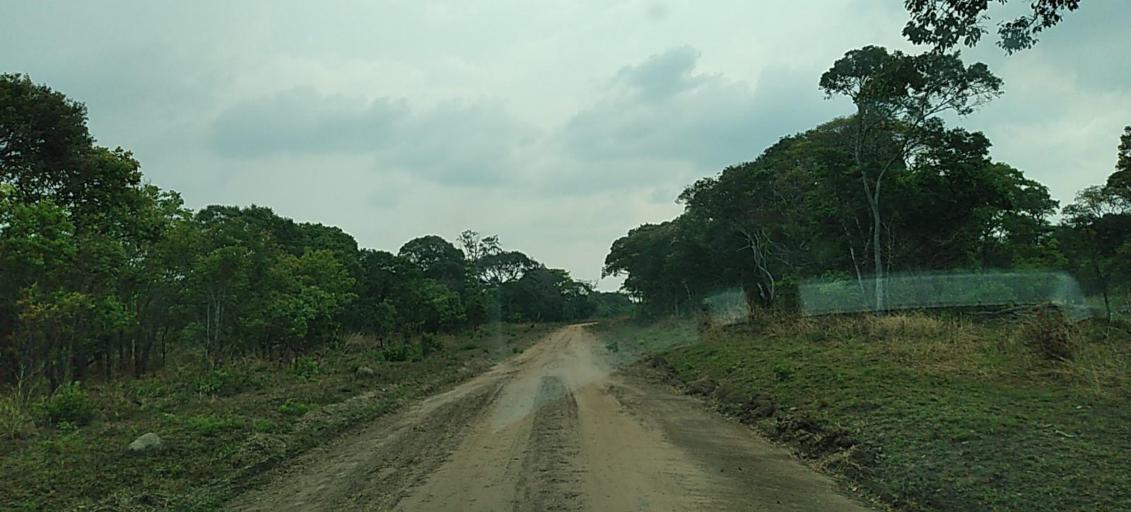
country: ZM
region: North-Western
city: Mwinilunga
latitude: -11.4113
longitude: 24.6179
